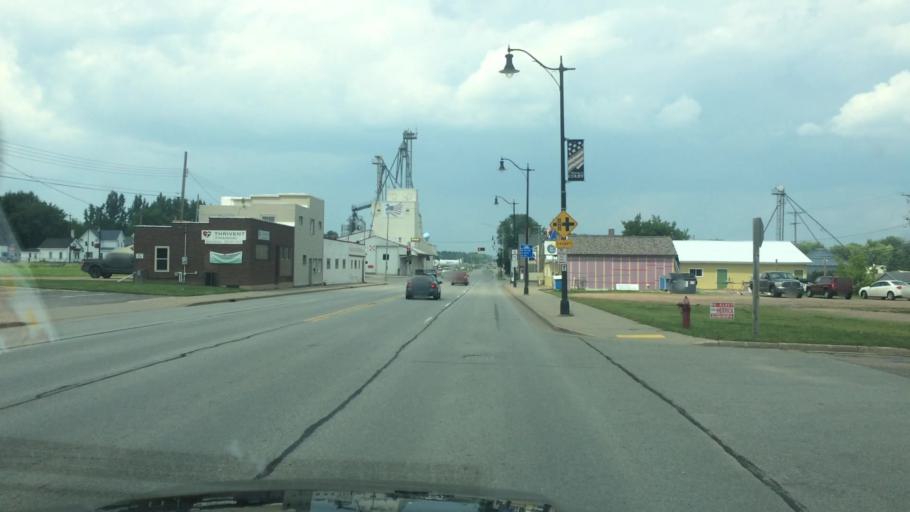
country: US
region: Wisconsin
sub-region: Clark County
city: Colby
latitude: 44.9083
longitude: -90.3153
